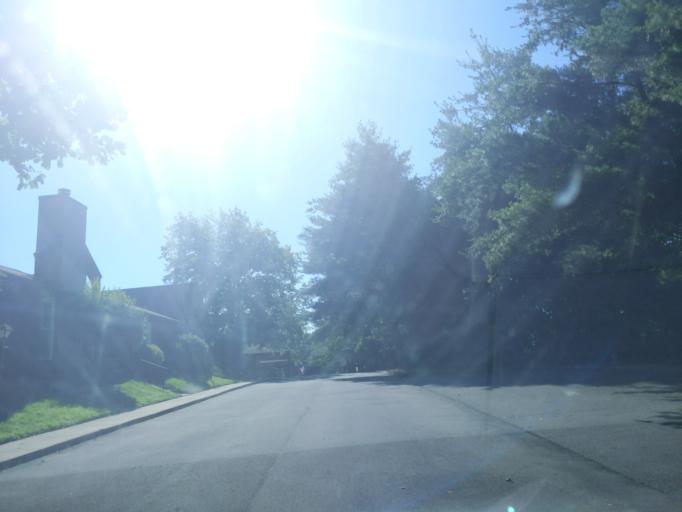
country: US
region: Tennessee
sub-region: Williamson County
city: Brentwood Estates
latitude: 36.0414
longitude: -86.7390
